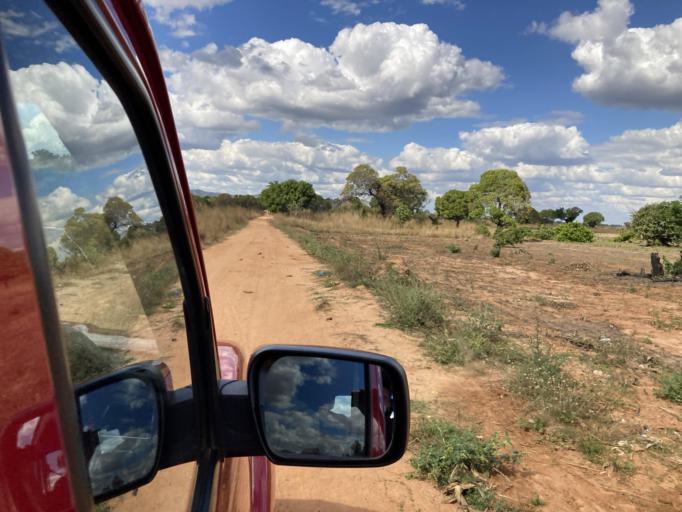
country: MZ
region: Cabo Delgado
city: Montepuez
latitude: -13.1262
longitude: 39.0401
